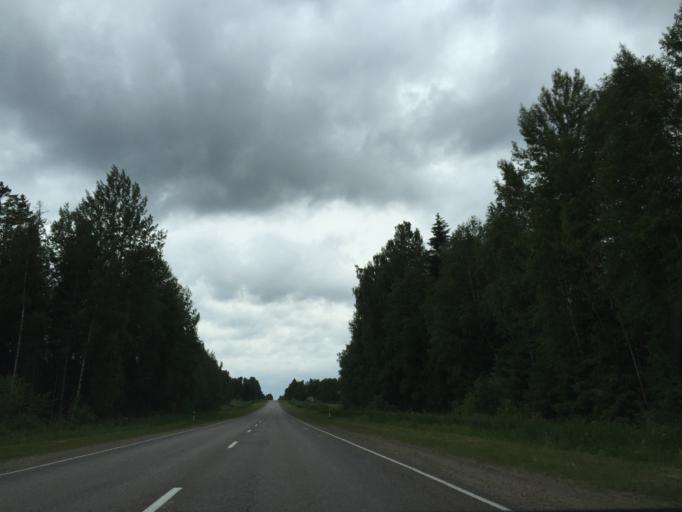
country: LV
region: Smiltene
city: Smiltene
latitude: 57.4018
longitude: 26.0303
